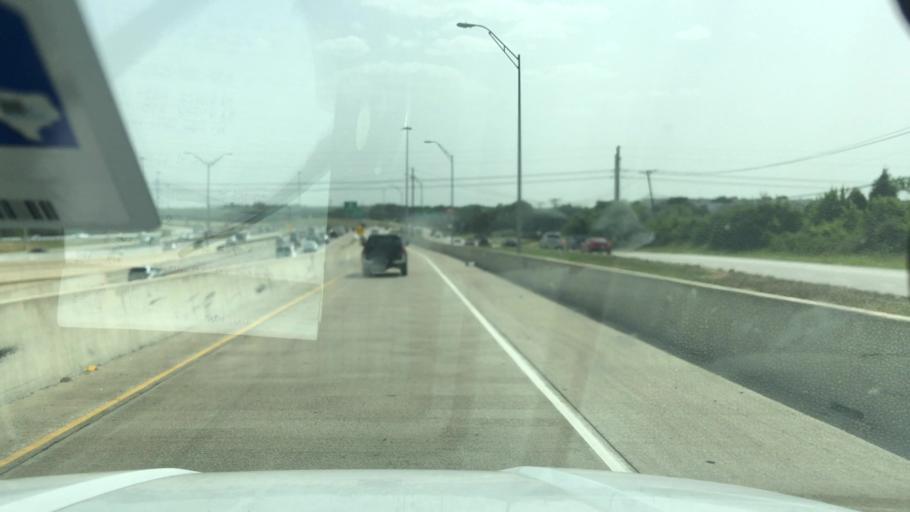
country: US
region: Texas
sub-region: Tarrant County
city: Grapevine
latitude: 32.9174
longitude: -97.0948
